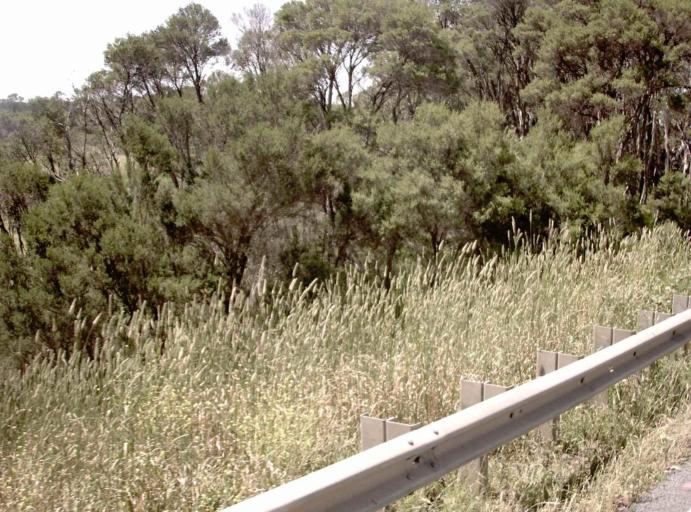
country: AU
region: Victoria
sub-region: Wellington
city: Heyfield
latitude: -38.1541
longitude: 146.7653
